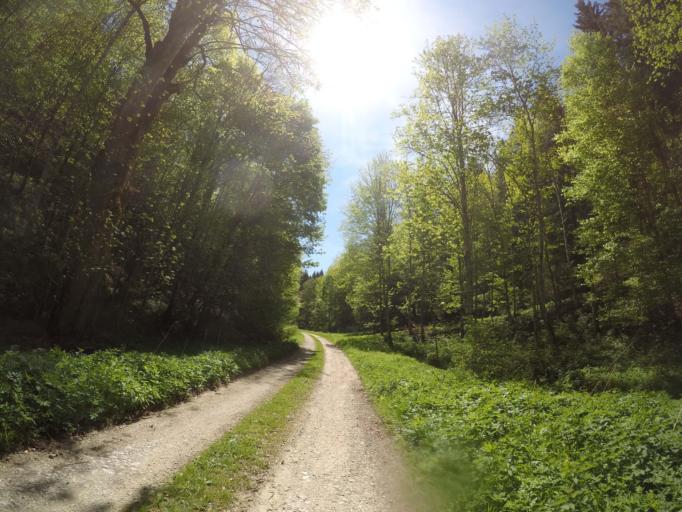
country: DE
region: Baden-Wuerttemberg
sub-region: Tuebingen Region
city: Schelklingen
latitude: 48.4124
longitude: 9.7191
